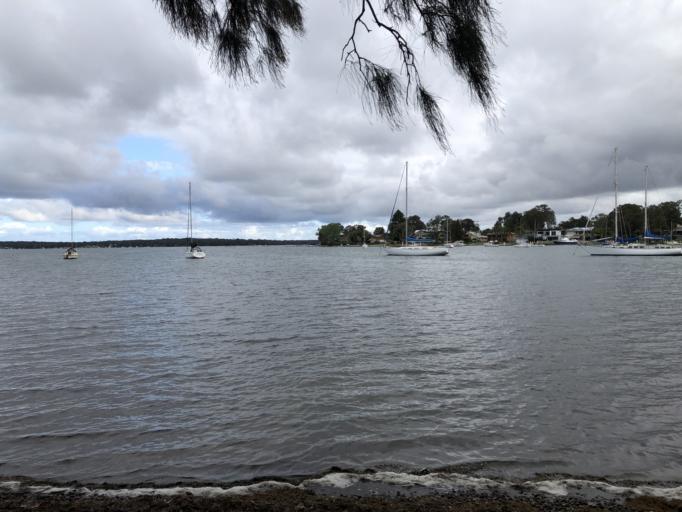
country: AU
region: New South Wales
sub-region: Wyong Shire
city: Kingfisher Shores
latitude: -33.1150
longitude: 151.5525
